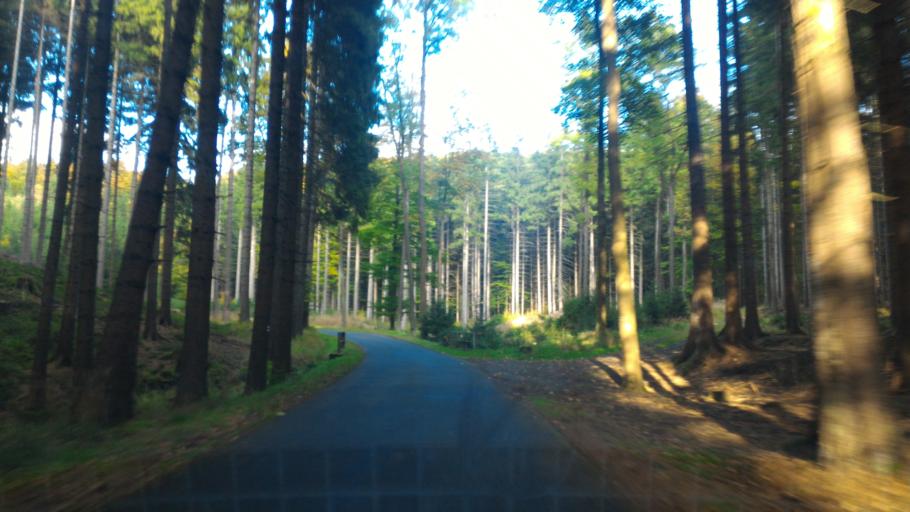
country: CZ
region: Ustecky
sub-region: Okres Decin
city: Chribska
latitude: 50.8201
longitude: 14.4895
